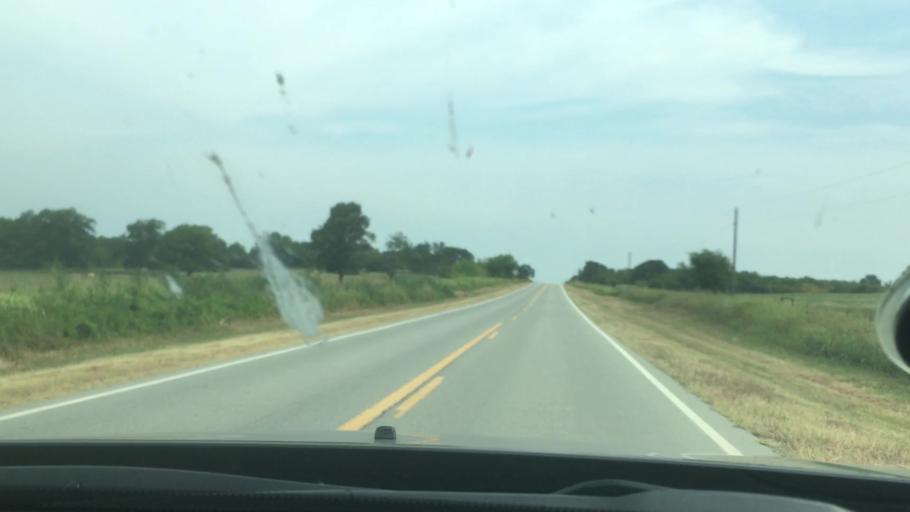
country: US
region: Oklahoma
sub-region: Coal County
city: Coalgate
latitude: 34.5519
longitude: -96.4070
